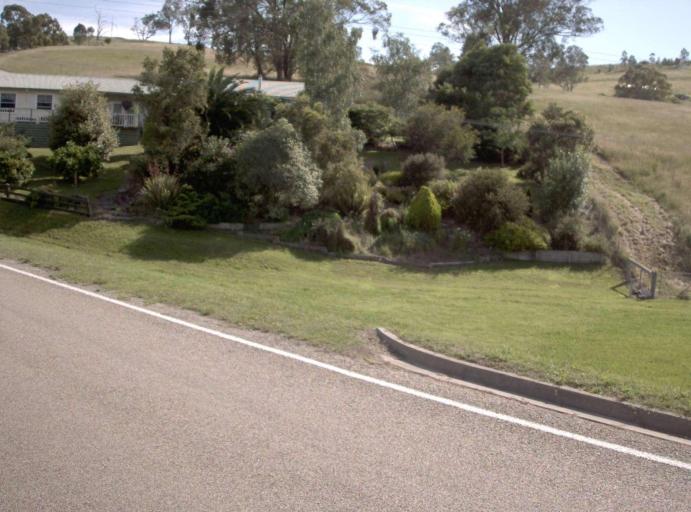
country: AU
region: Victoria
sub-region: East Gippsland
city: Lakes Entrance
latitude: -37.4949
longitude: 148.1740
